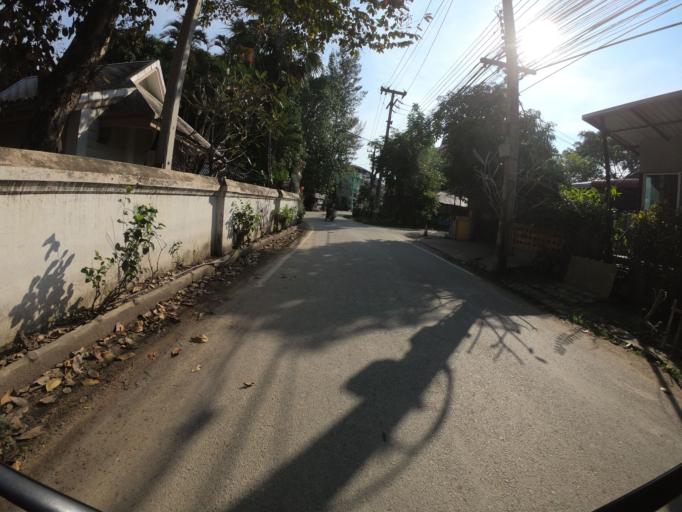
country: TH
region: Chiang Mai
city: Chiang Mai
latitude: 18.8457
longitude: 98.9773
